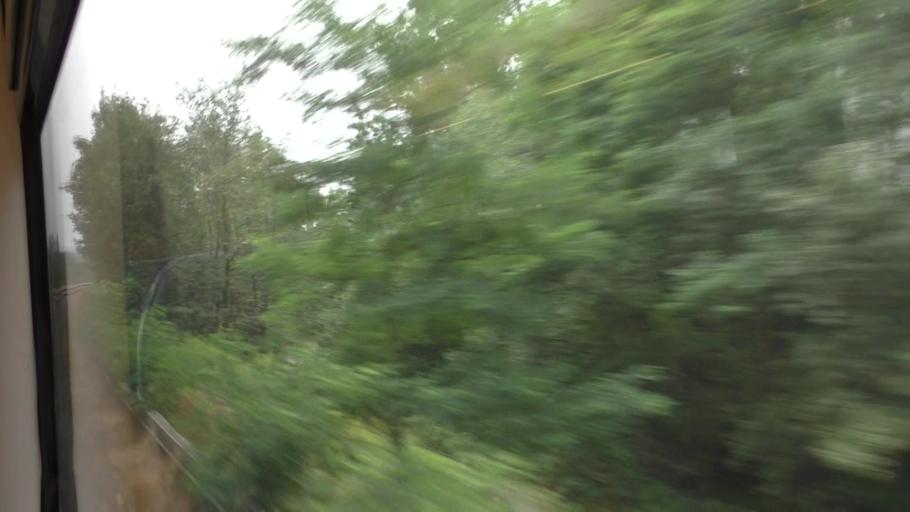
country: DE
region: Saxony
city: Goerlitz
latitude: 51.1132
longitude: 14.9745
